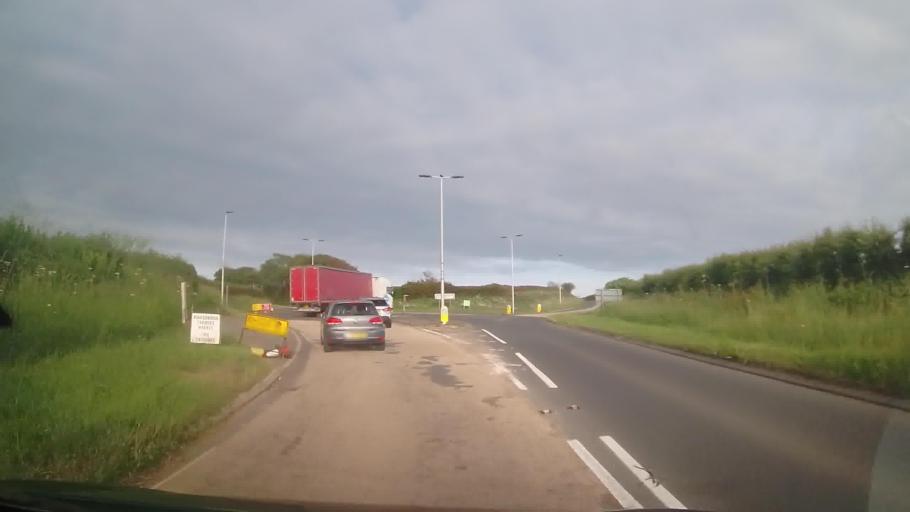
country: GB
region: England
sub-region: Devon
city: Kingsbridge
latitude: 50.2976
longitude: -3.7986
